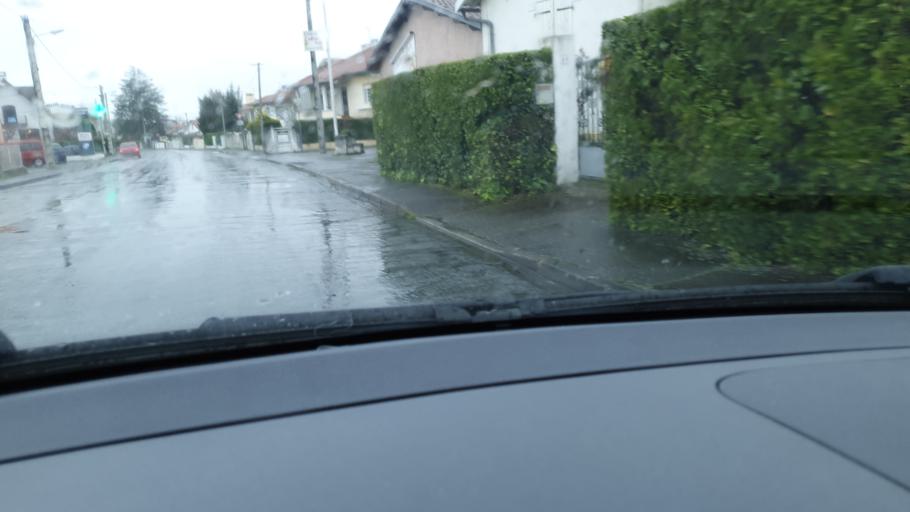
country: FR
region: Midi-Pyrenees
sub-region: Departement des Hautes-Pyrenees
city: Tarbes
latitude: 43.2427
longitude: 0.0541
